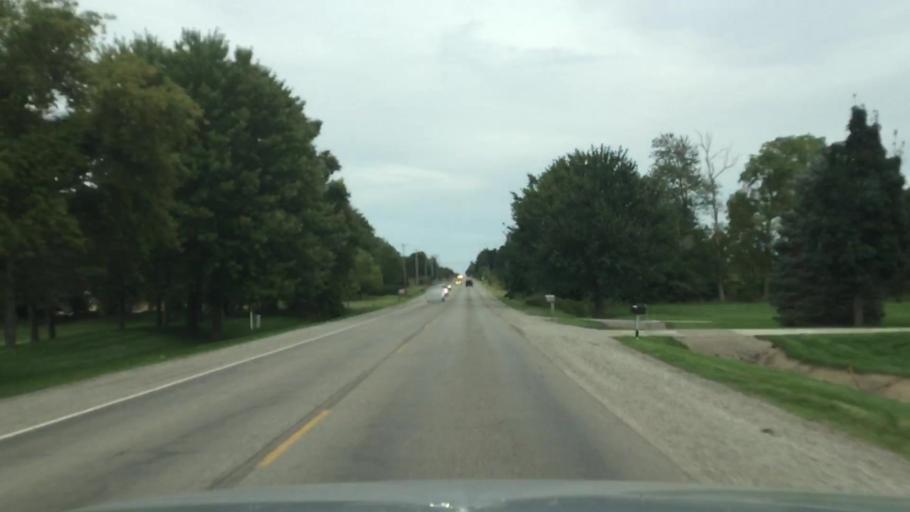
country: US
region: Michigan
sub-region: Genesee County
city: Grand Blanc
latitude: 42.8861
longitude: -83.6665
